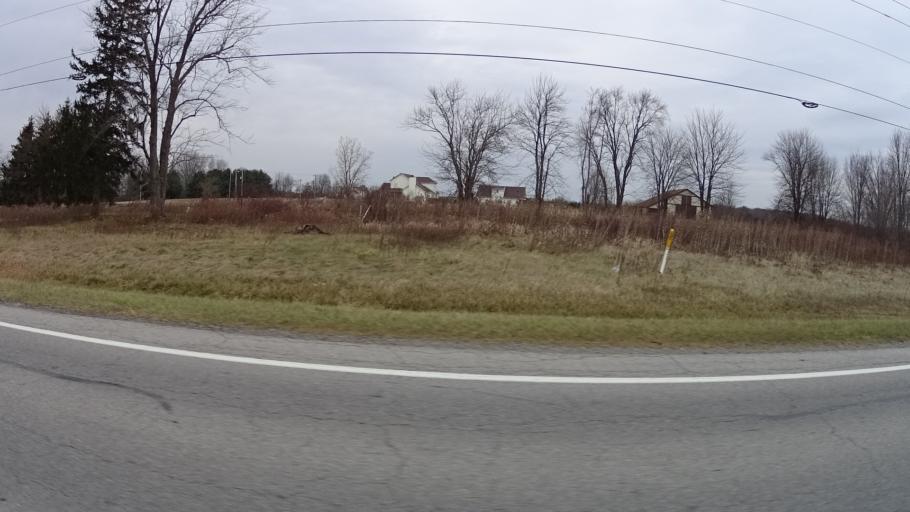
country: US
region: Ohio
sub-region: Lorain County
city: Wellington
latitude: 41.1688
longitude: -82.1683
